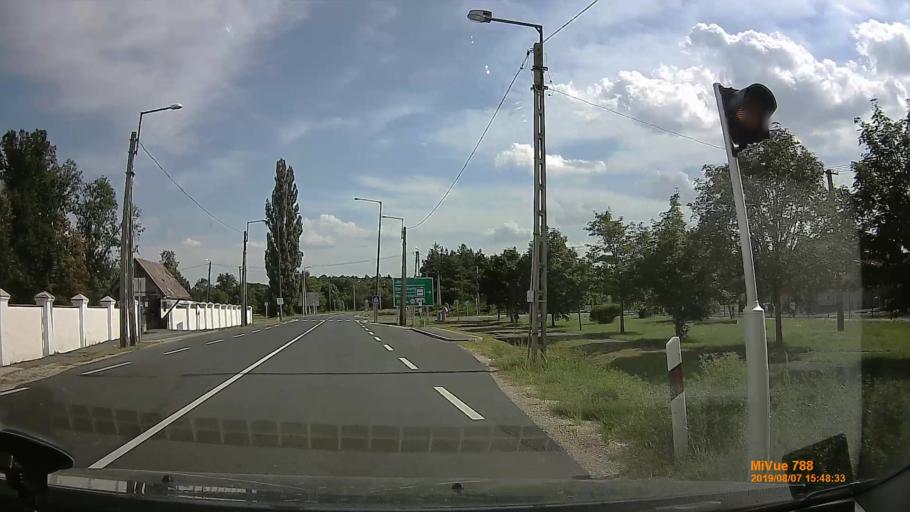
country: HU
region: Vas
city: Jak
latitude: 47.1603
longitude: 16.6378
